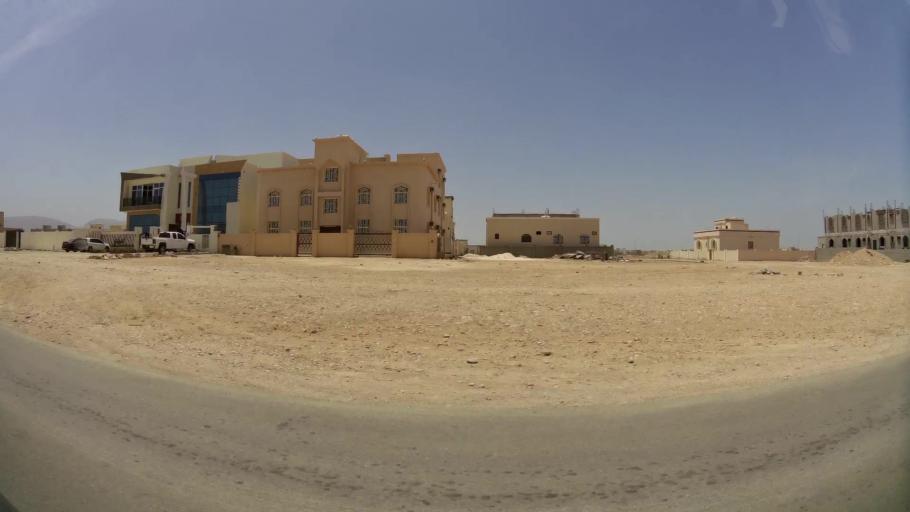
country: OM
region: Zufar
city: Salalah
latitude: 17.0860
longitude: 54.1969
